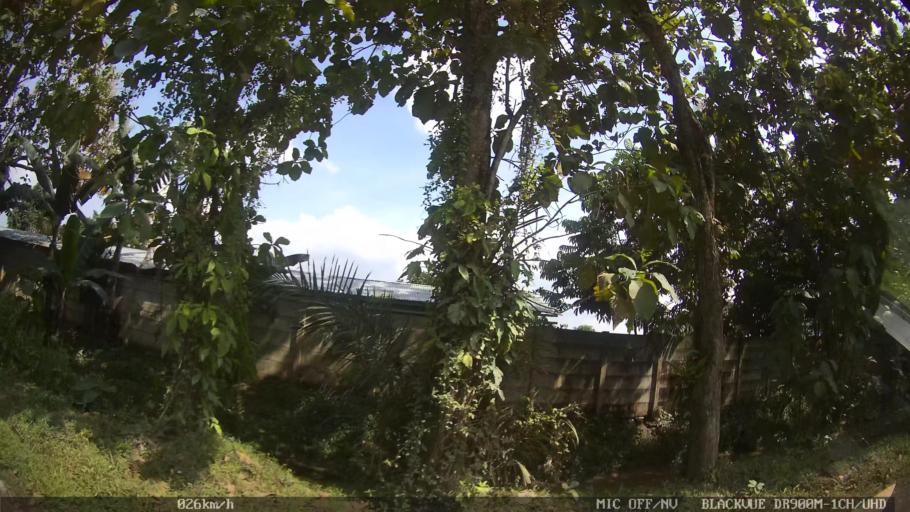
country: ID
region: North Sumatra
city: Binjai
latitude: 3.6346
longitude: 98.5295
